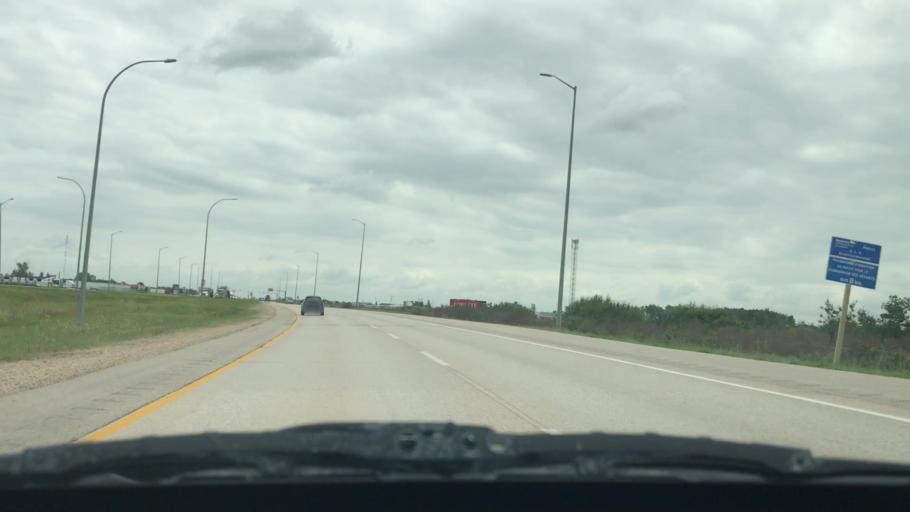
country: CA
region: Manitoba
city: Winnipeg
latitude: 49.8238
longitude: -96.9446
